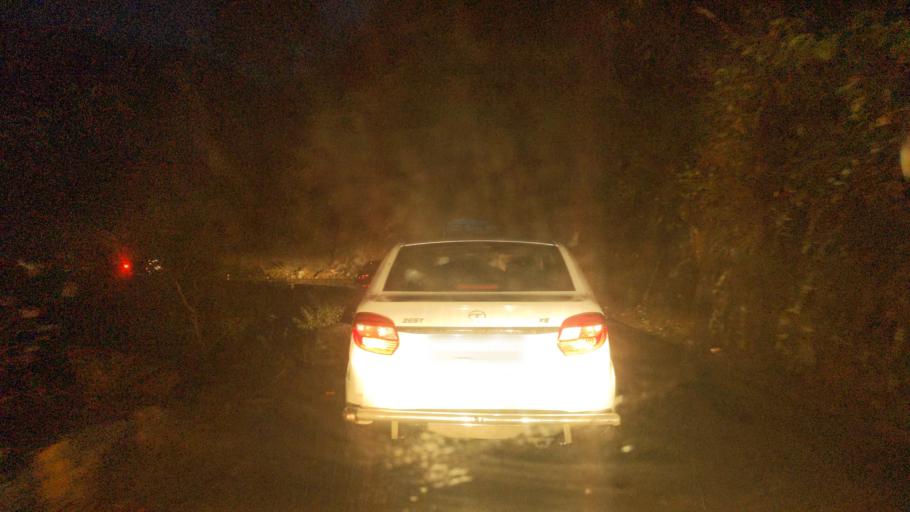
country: IN
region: Uttarakhand
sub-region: Naini Tal
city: Haldwani
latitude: 29.2785
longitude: 79.5450
